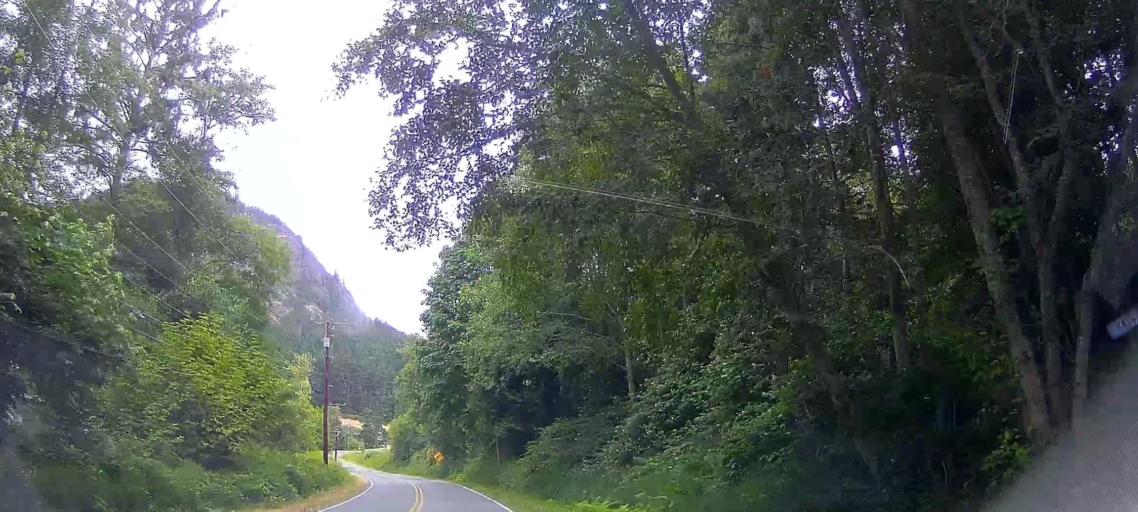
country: US
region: Washington
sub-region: Skagit County
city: Anacortes
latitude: 48.4488
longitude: -122.6388
